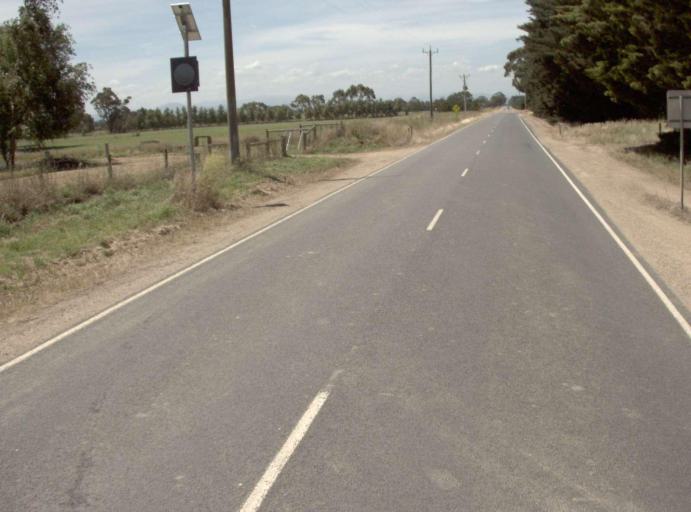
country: AU
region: Victoria
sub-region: Wellington
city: Heyfield
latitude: -38.0565
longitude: 146.8737
